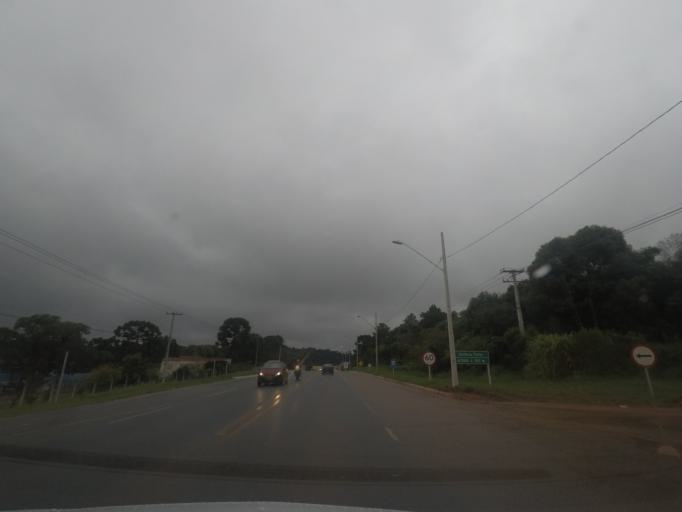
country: BR
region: Parana
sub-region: Colombo
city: Colombo
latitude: -25.3430
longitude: -49.1588
